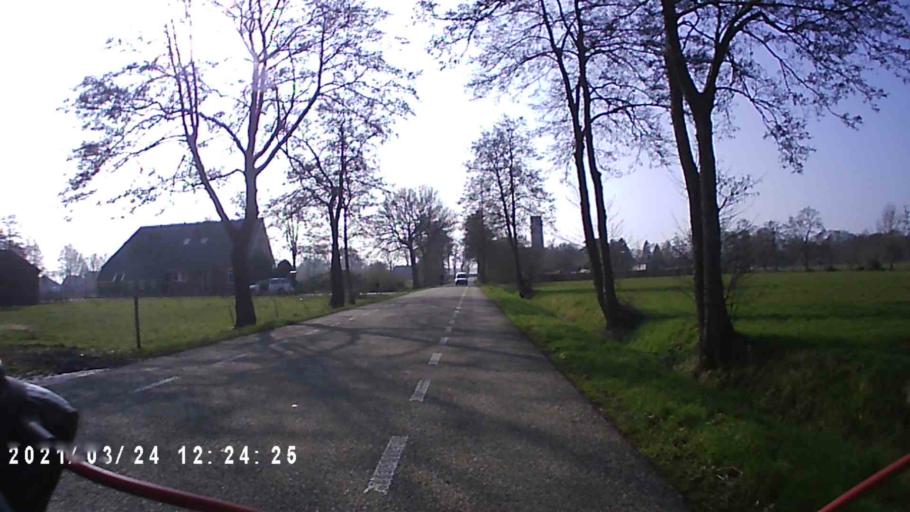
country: NL
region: Groningen
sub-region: Gemeente Leek
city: Leek
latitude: 53.1833
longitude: 6.3929
